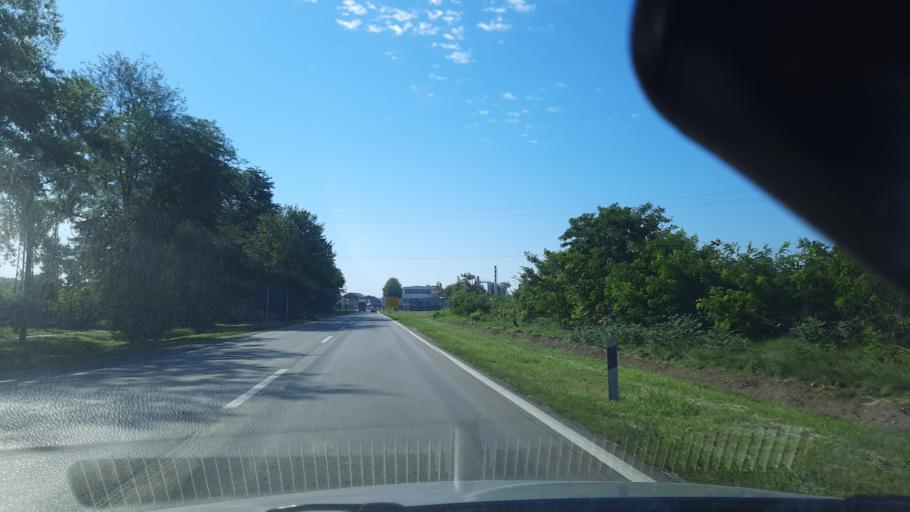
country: RS
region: Autonomna Pokrajina Vojvodina
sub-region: Juznobanatski Okrug
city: Kovin
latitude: 44.7561
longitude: 20.9645
